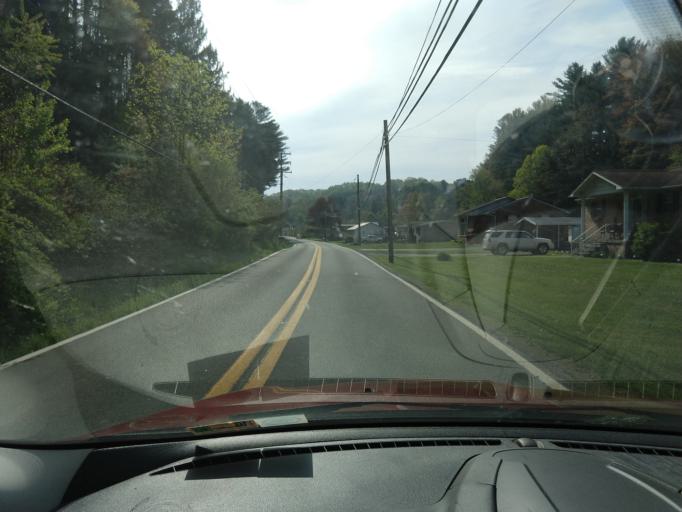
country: US
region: West Virginia
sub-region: Raleigh County
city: Crab Orchard
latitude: 37.7406
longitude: -81.2384
